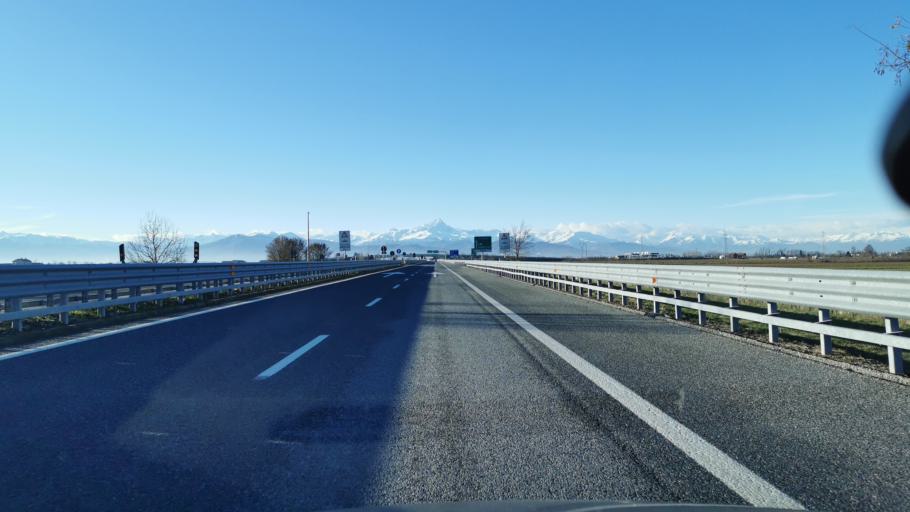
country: IT
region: Piedmont
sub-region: Provincia di Cuneo
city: Montanera
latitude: 44.4734
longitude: 7.7012
